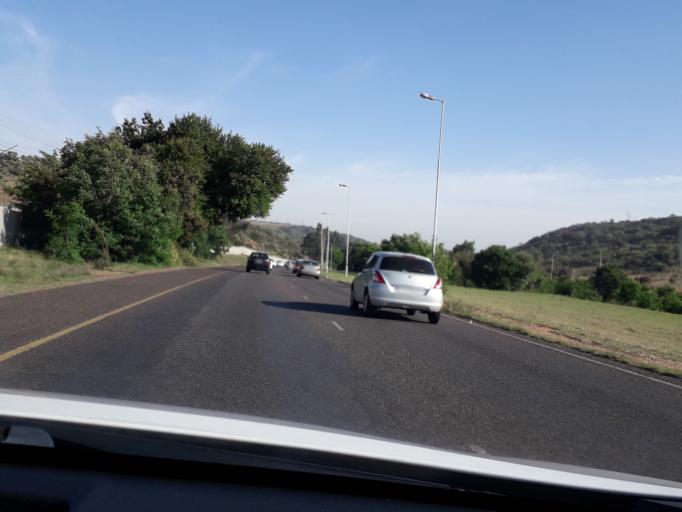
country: ZA
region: Gauteng
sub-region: City of Tshwane Metropolitan Municipality
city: Centurion
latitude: -25.8063
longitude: 28.1989
